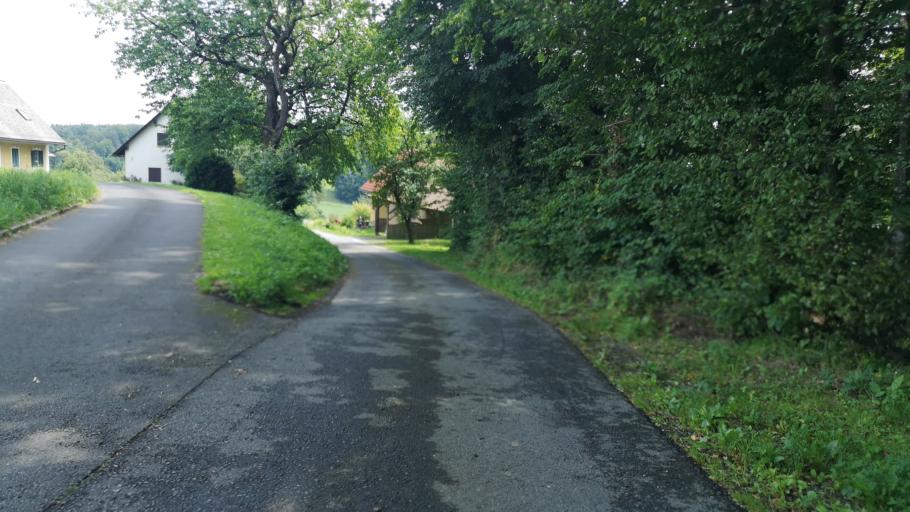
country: AT
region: Styria
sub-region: Politischer Bezirk Leibnitz
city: Weitendorf
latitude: 46.8722
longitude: 15.4619
